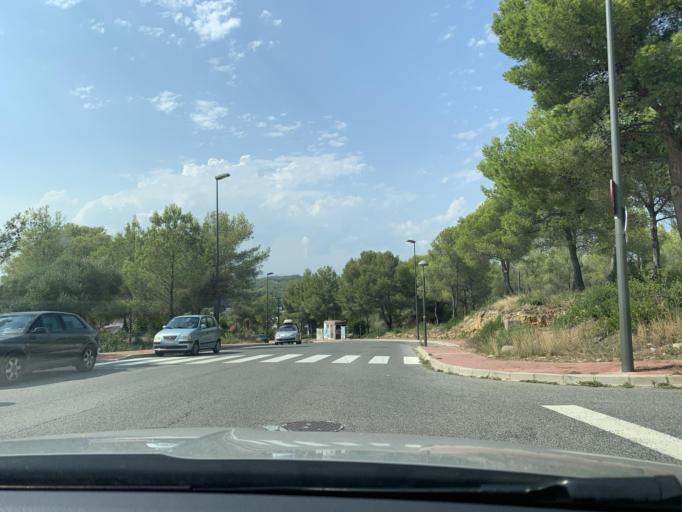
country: ES
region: Catalonia
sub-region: Provincia de Tarragona
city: Altafulla
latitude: 41.1366
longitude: 1.3518
